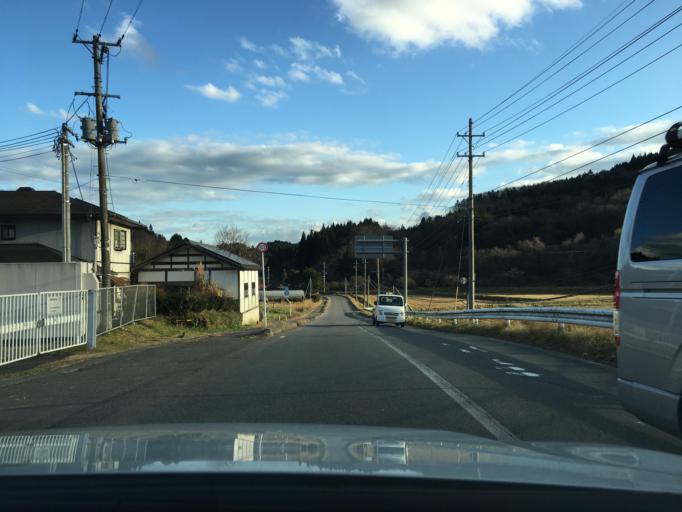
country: JP
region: Fukushima
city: Ishikawa
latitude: 37.1967
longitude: 140.6260
